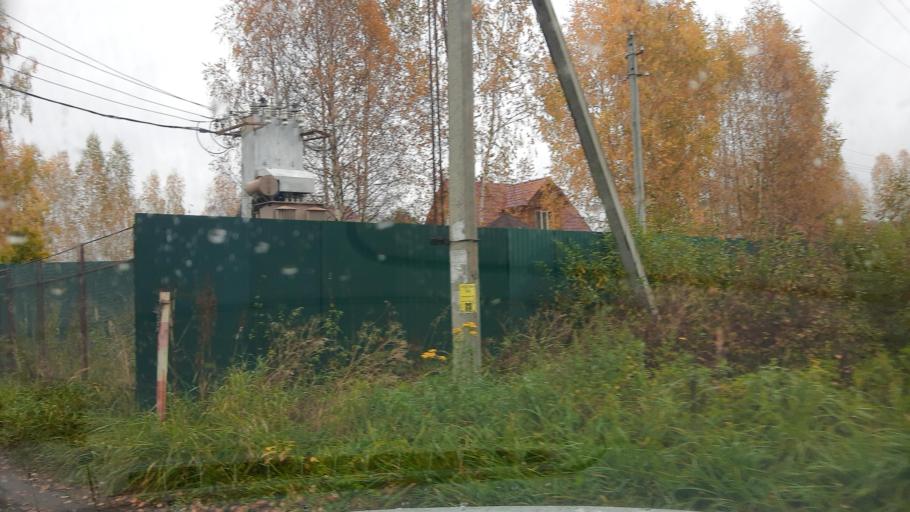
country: RU
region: Moskovskaya
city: Imeni Vorovskogo
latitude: 55.7818
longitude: 38.3638
